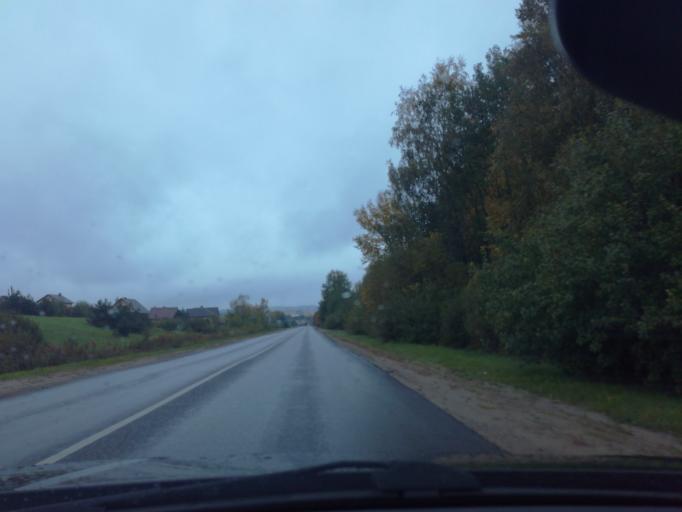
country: LT
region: Alytaus apskritis
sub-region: Alytus
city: Alytus
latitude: 54.4058
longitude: 24.0792
